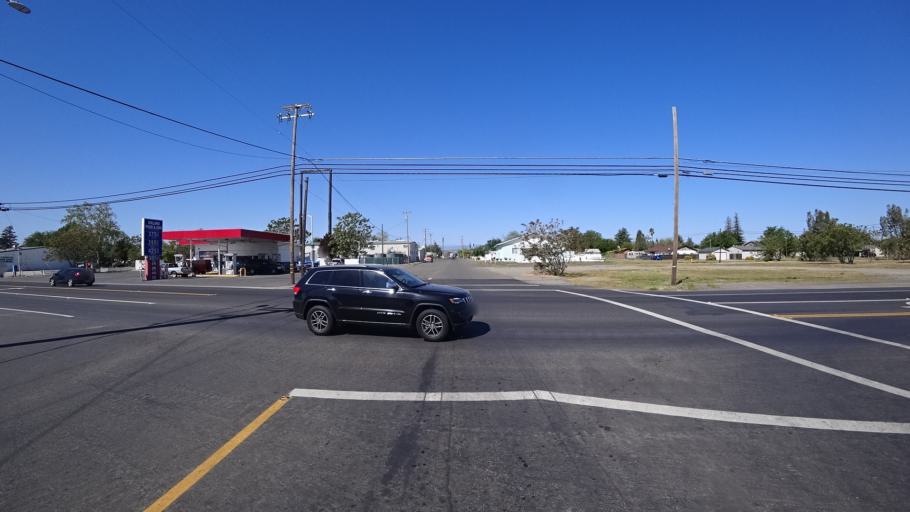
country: US
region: California
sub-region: Glenn County
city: Orland
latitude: 39.7496
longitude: -122.1973
